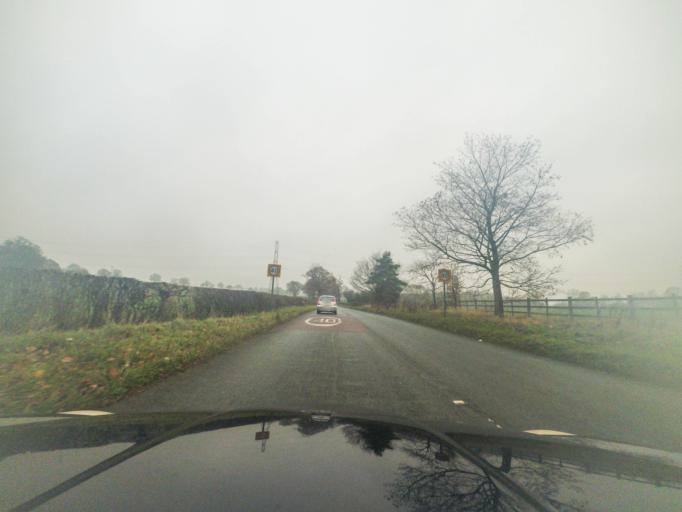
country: GB
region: England
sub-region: Solihull
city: Barston
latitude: 52.3899
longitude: -1.6871
